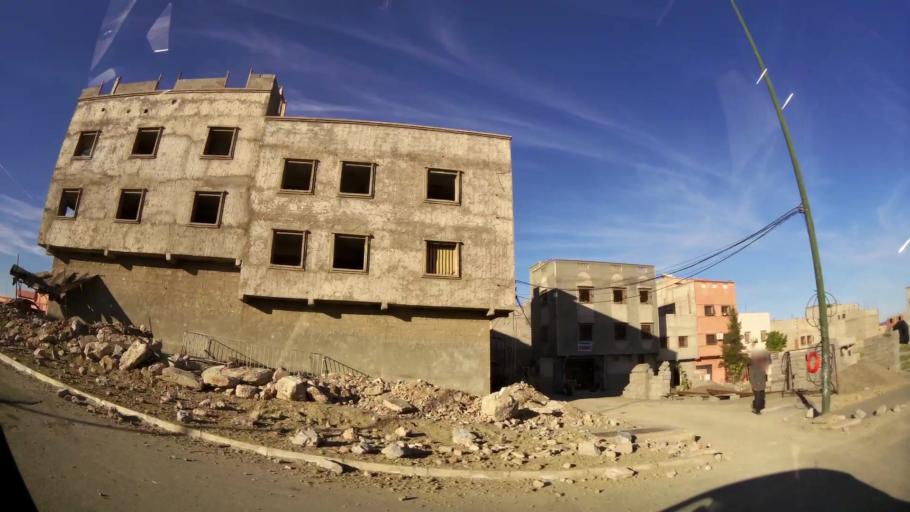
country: MA
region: Marrakech-Tensift-Al Haouz
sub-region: Marrakech
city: Marrakesh
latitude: 31.7659
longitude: -8.0970
